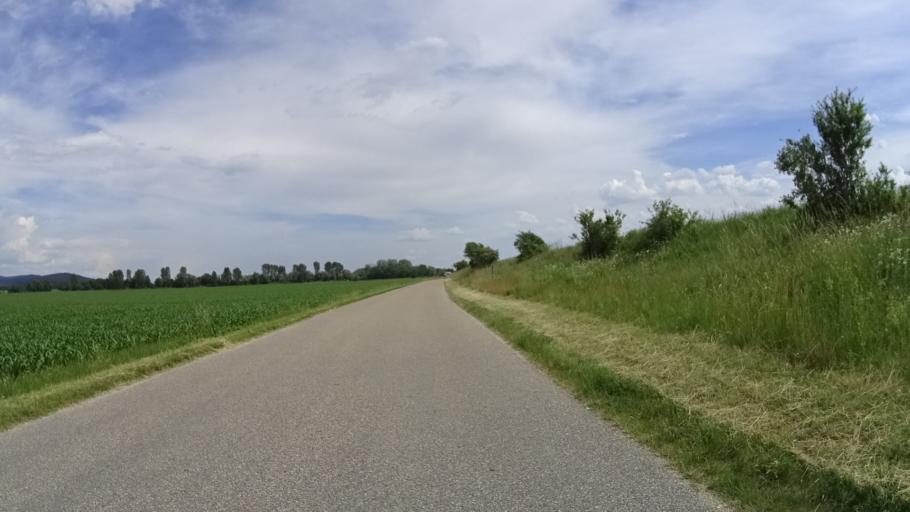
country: DE
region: Bavaria
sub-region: Upper Palatinate
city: Wiesent
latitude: 49.0113
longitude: 12.3281
